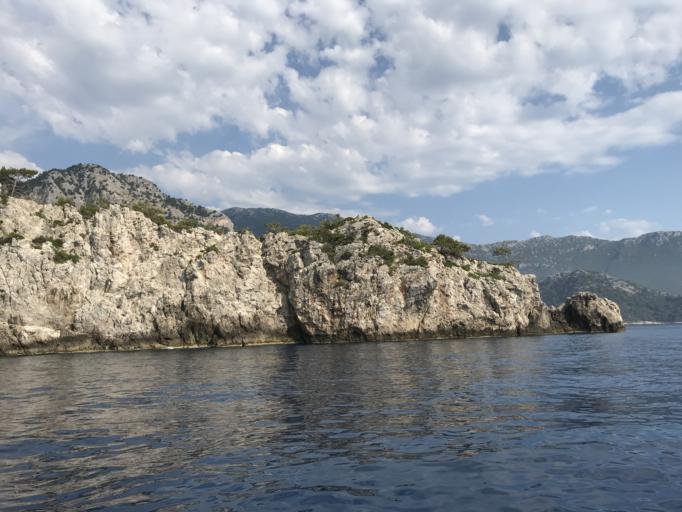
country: TR
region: Mugla
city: OEluedeniz
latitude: 36.4436
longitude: 29.1209
